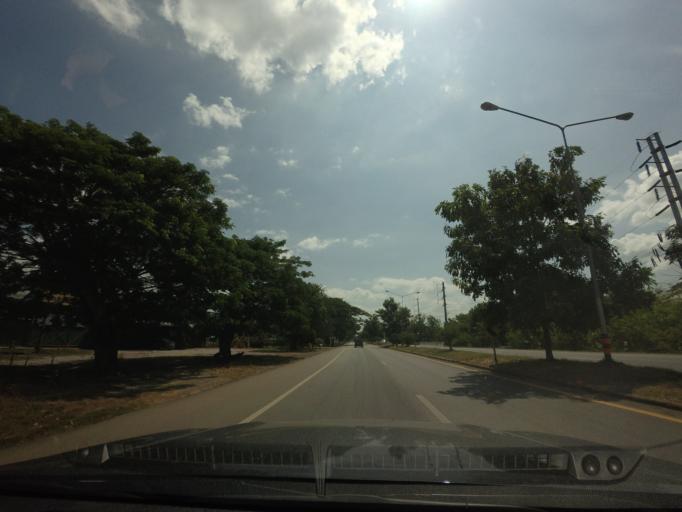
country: TH
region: Phetchabun
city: Nong Phai
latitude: 15.9404
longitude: 101.0293
